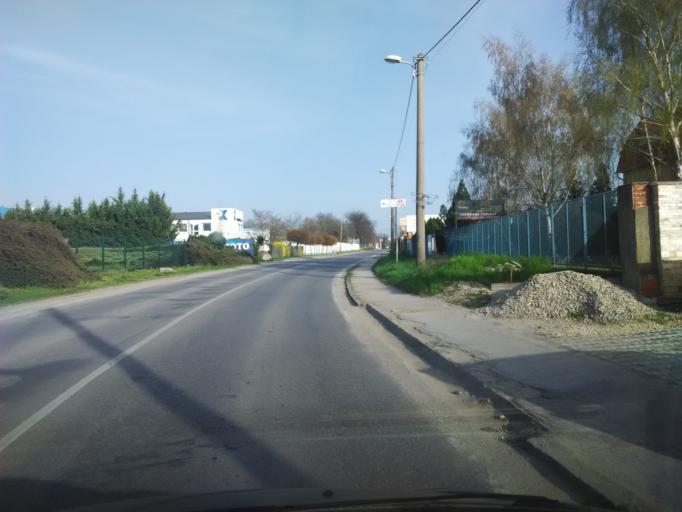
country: SK
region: Nitriansky
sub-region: Okres Nove Zamky
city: Nove Zamky
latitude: 48.0042
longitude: 18.1621
